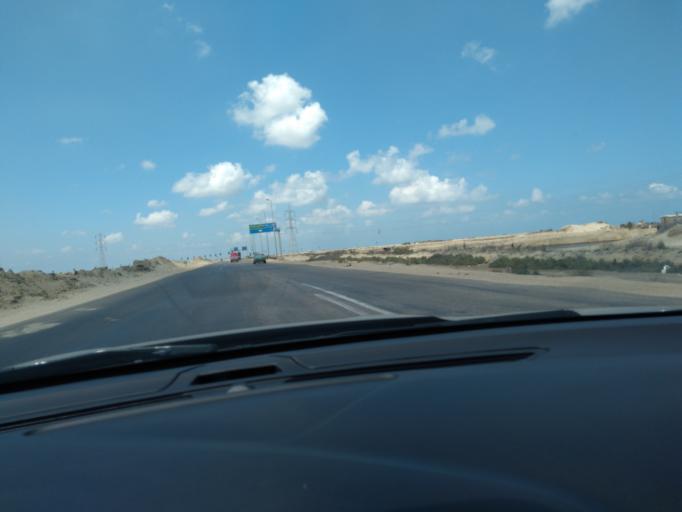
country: EG
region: Muhafazat ad Daqahliyah
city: Al Matariyah
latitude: 31.3497
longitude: 32.0546
